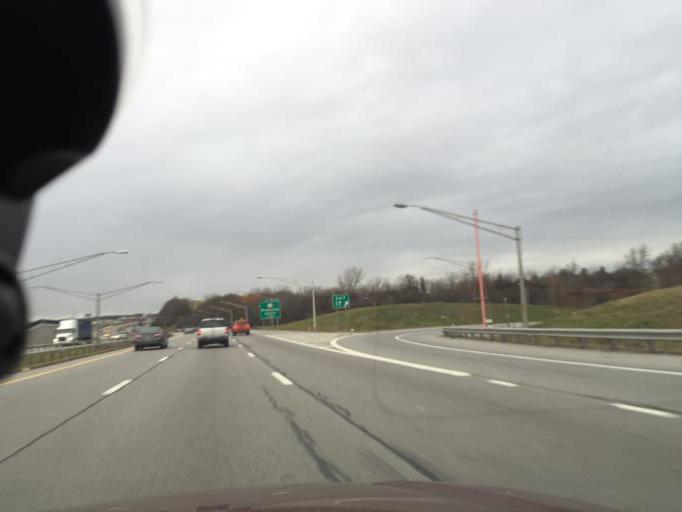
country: US
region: New York
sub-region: Monroe County
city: Rochester
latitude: 43.1233
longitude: -77.6491
